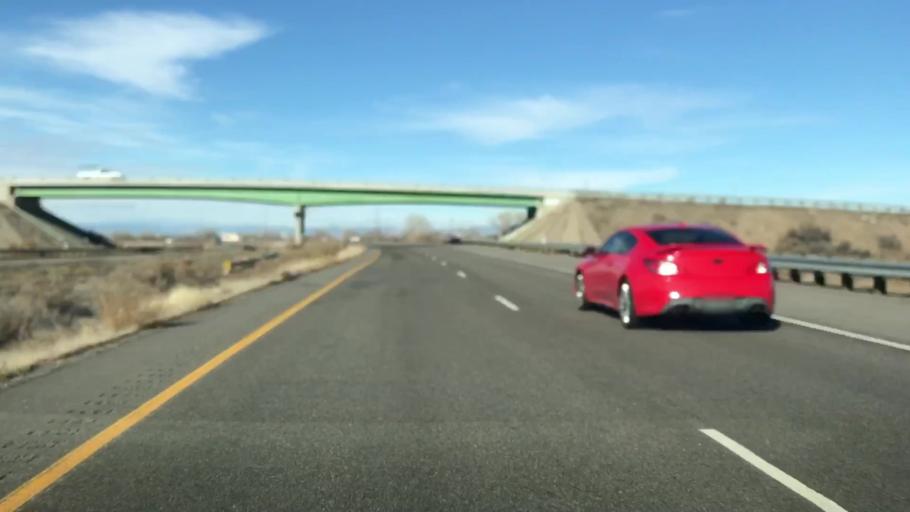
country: US
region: Colorado
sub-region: Mesa County
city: Fruita
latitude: 39.1274
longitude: -108.6832
